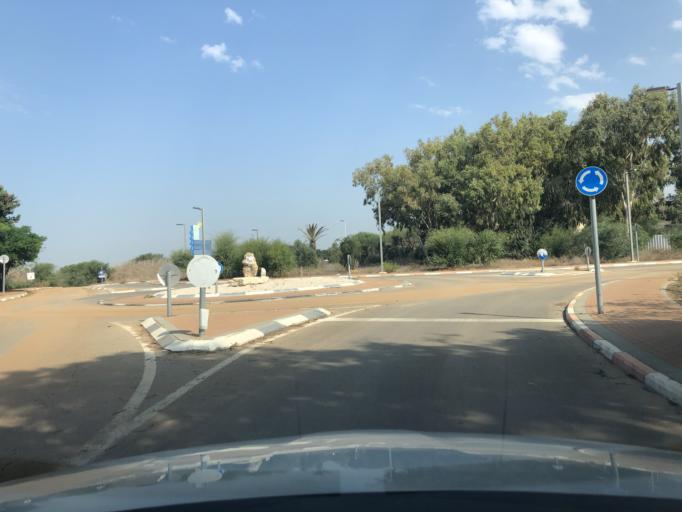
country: IL
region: Tel Aviv
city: Kefar Shemaryahu
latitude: 32.2150
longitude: 34.8186
